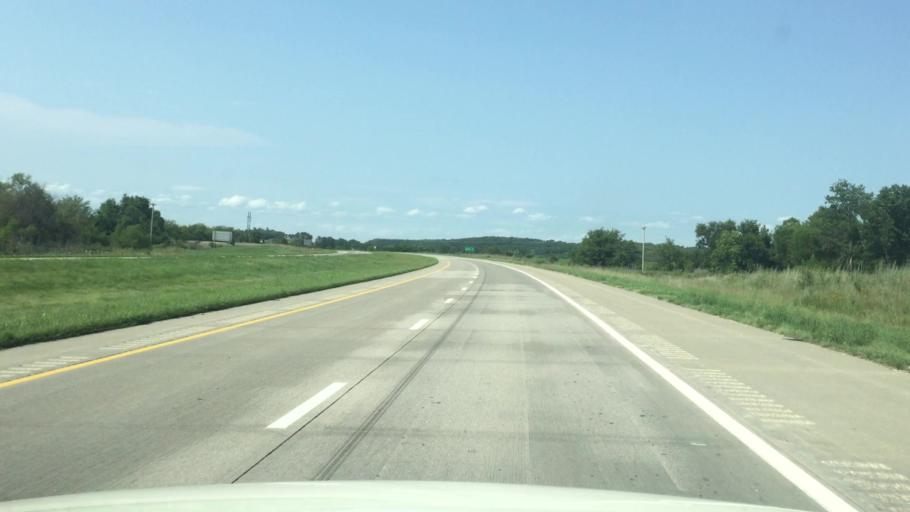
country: US
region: Kansas
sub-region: Linn County
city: Pleasanton
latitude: 38.2708
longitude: -94.6682
